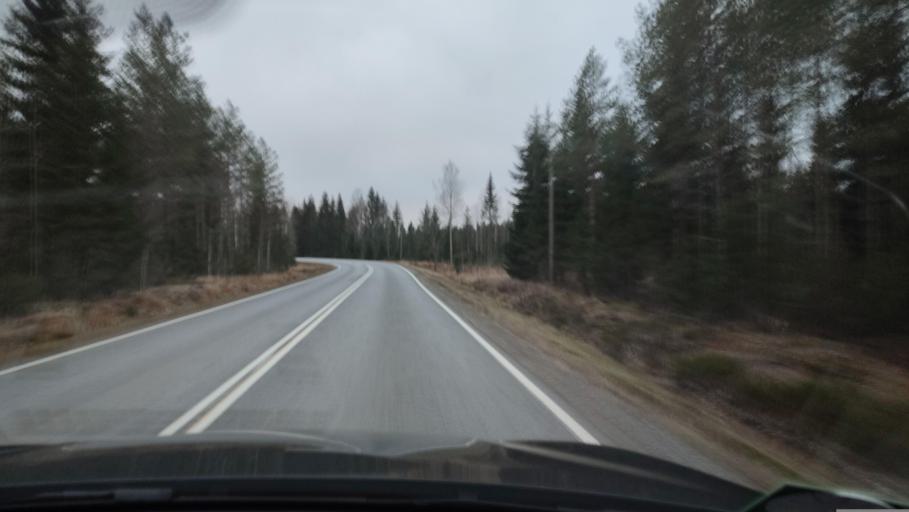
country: FI
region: Southern Ostrobothnia
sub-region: Suupohja
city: Karijoki
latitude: 62.3298
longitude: 21.8996
